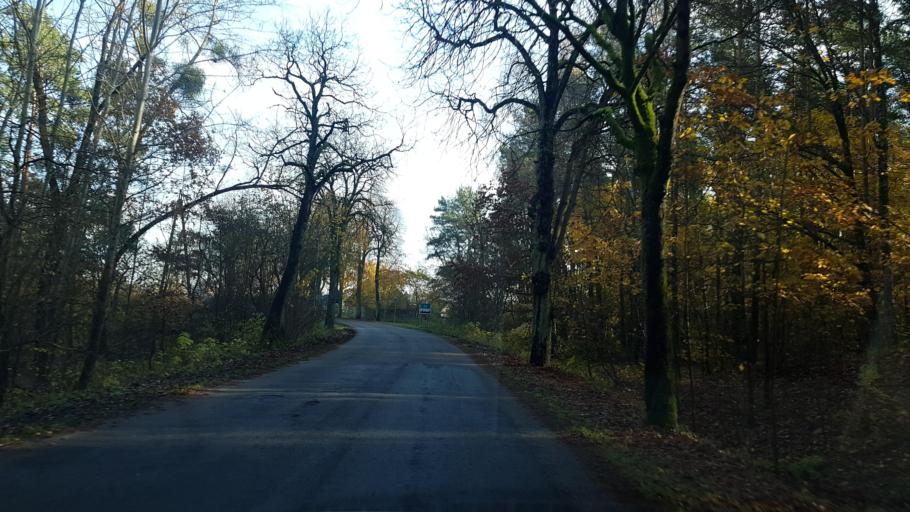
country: PL
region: West Pomeranian Voivodeship
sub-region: Powiat policki
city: Dobra
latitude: 53.4990
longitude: 14.3489
